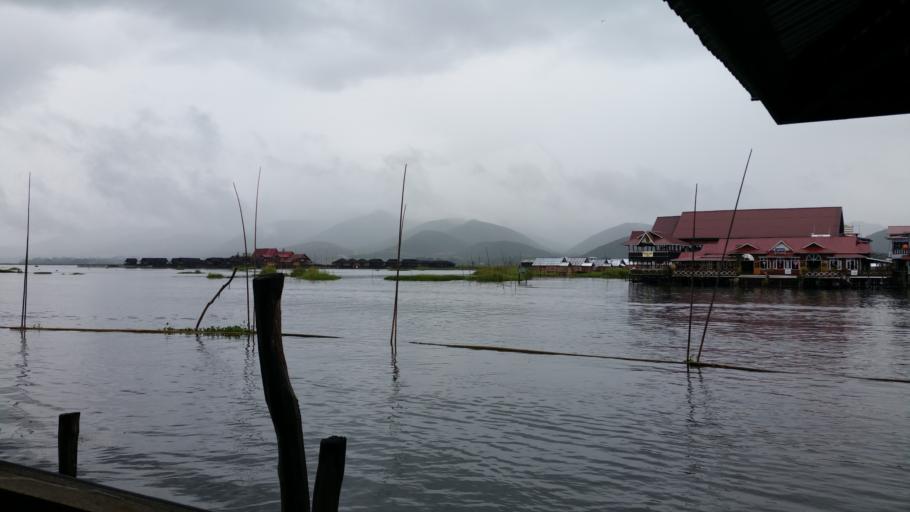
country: MM
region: Shan
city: Taunggyi
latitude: 20.4577
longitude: 96.9046
